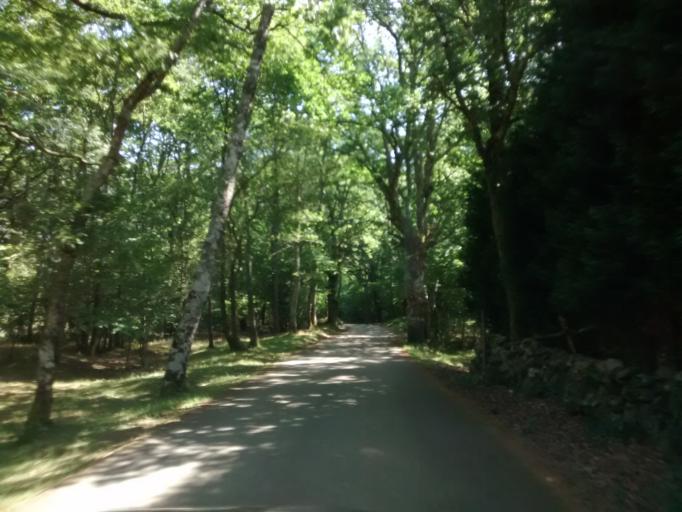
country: ES
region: Cantabria
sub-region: Provincia de Cantabria
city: Ruente
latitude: 43.2359
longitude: -4.2232
